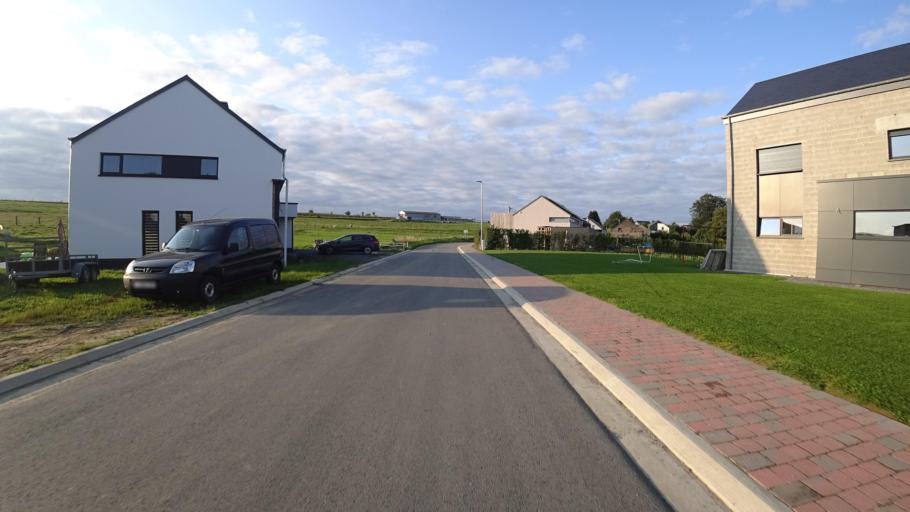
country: BE
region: Wallonia
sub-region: Province du Luxembourg
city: Neufchateau
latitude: 49.8902
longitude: 5.3838
